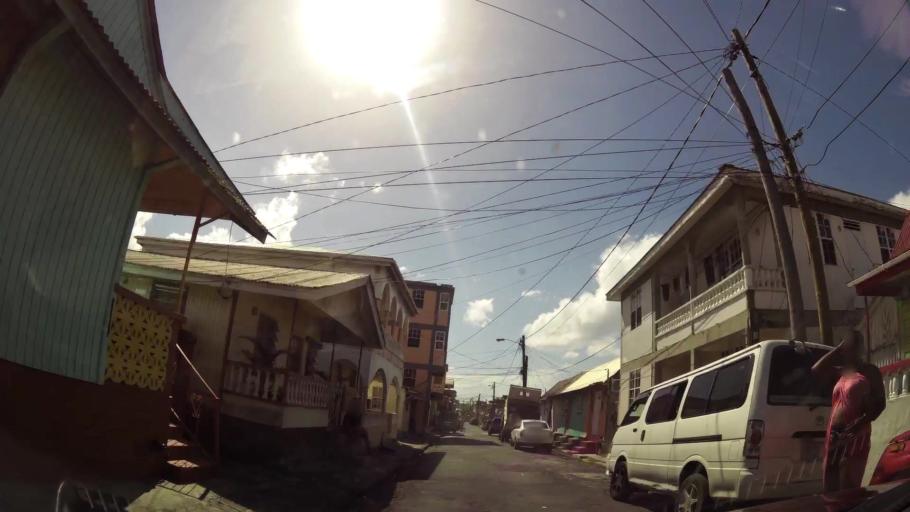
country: DM
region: Saint George
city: Roseau
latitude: 15.3017
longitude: -61.3869
